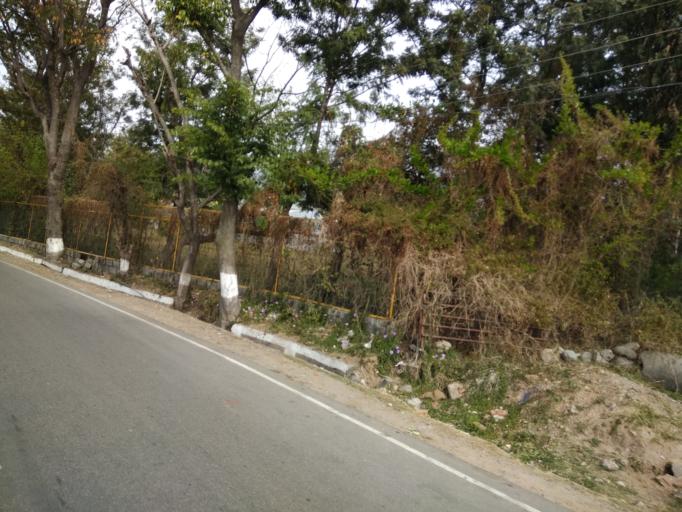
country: IN
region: Himachal Pradesh
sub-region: Kangra
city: Dharmsala
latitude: 32.1935
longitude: 76.3474
